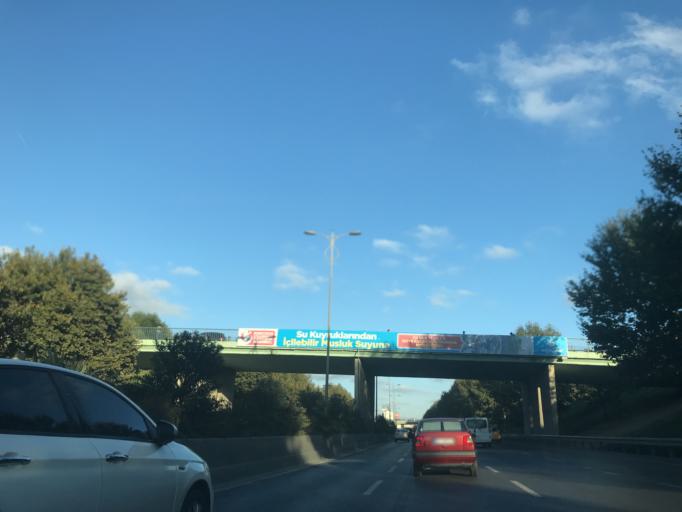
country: TR
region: Istanbul
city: Bagcilar
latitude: 41.0551
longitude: 28.8538
